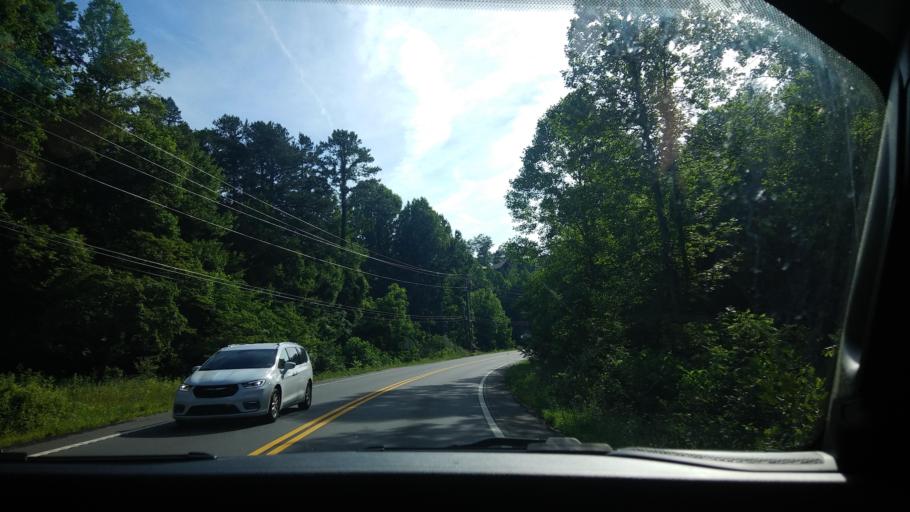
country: US
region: Tennessee
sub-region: Sevier County
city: Gatlinburg
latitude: 35.7508
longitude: -83.3936
